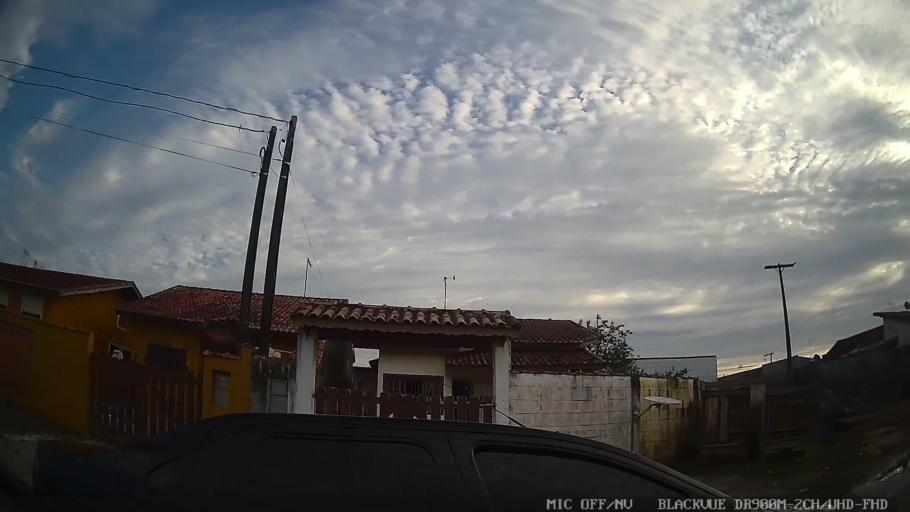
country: BR
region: Sao Paulo
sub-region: Itanhaem
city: Itanhaem
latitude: -24.1677
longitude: -46.7718
